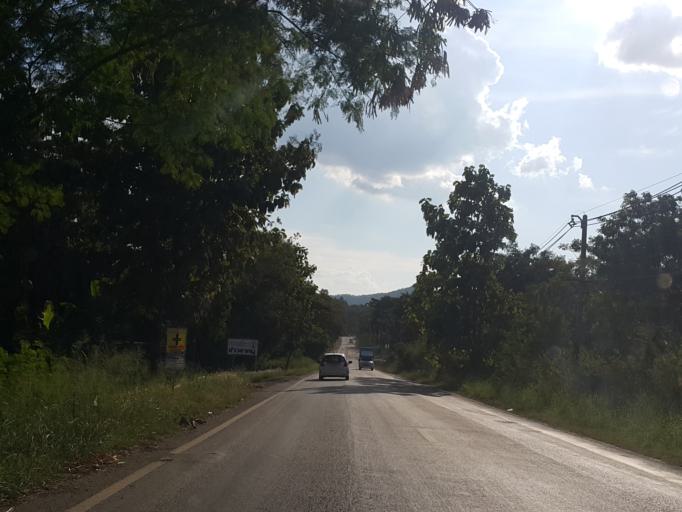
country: TH
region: Chiang Mai
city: Mae On
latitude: 18.8144
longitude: 99.2539
